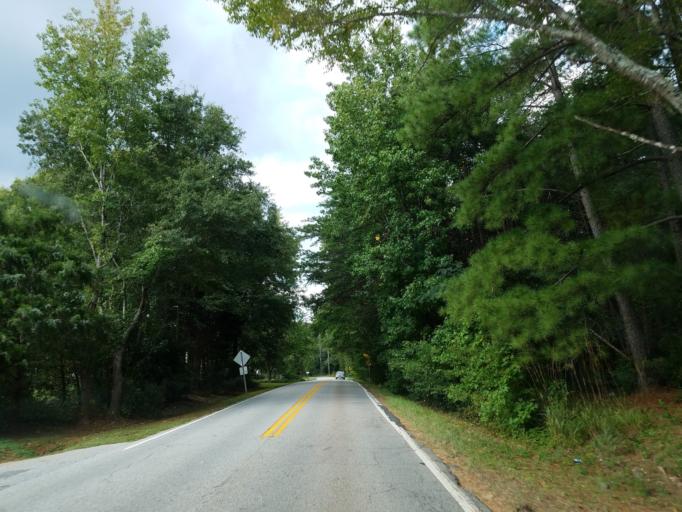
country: US
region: South Carolina
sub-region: Greenville County
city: Taylors
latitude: 34.8574
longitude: -82.2815
